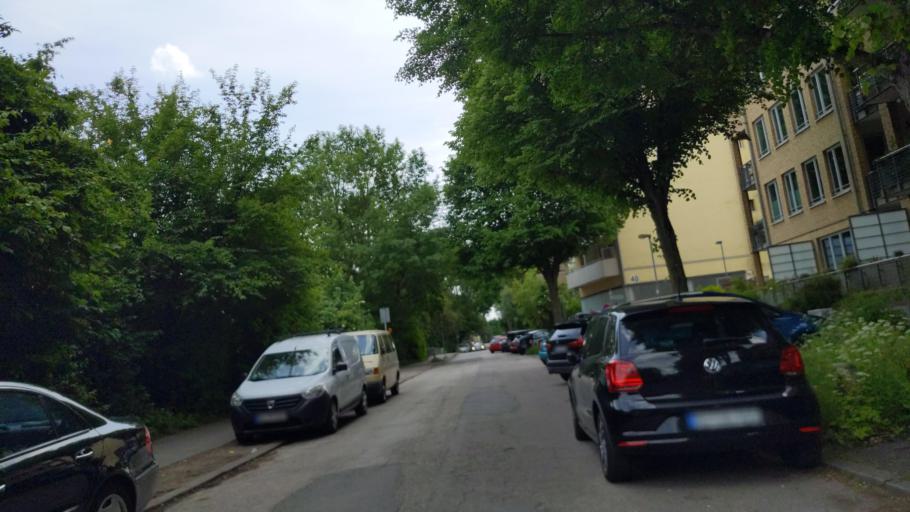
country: DE
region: Schleswig-Holstein
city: Luebeck
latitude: 53.8650
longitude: 10.7032
